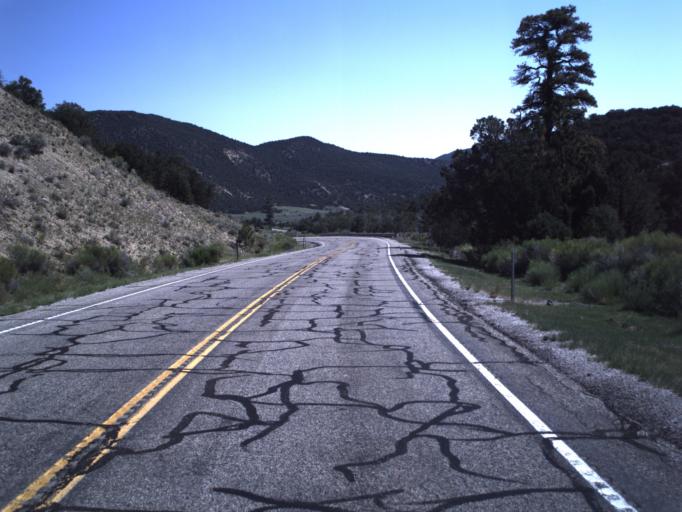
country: US
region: Utah
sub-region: Wayne County
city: Loa
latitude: 38.6612
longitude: -111.4302
